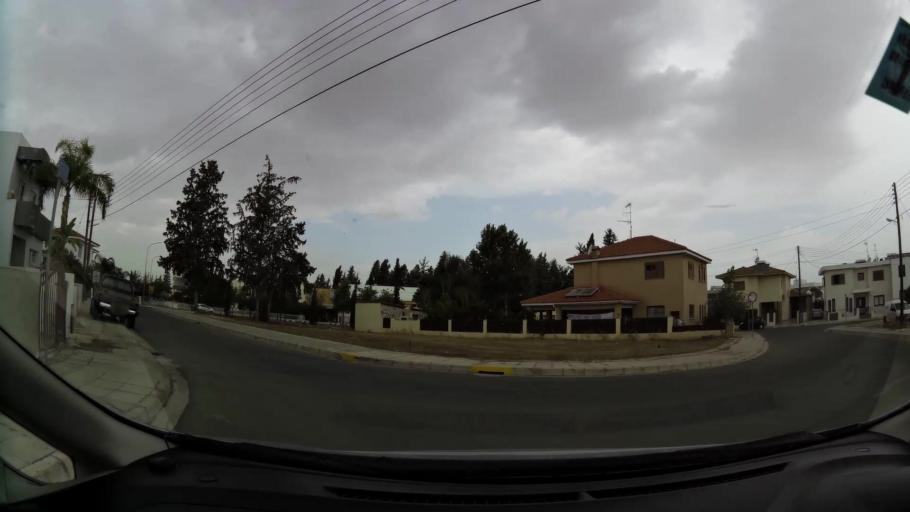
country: CY
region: Lefkosia
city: Geri
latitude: 35.0964
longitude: 33.3829
